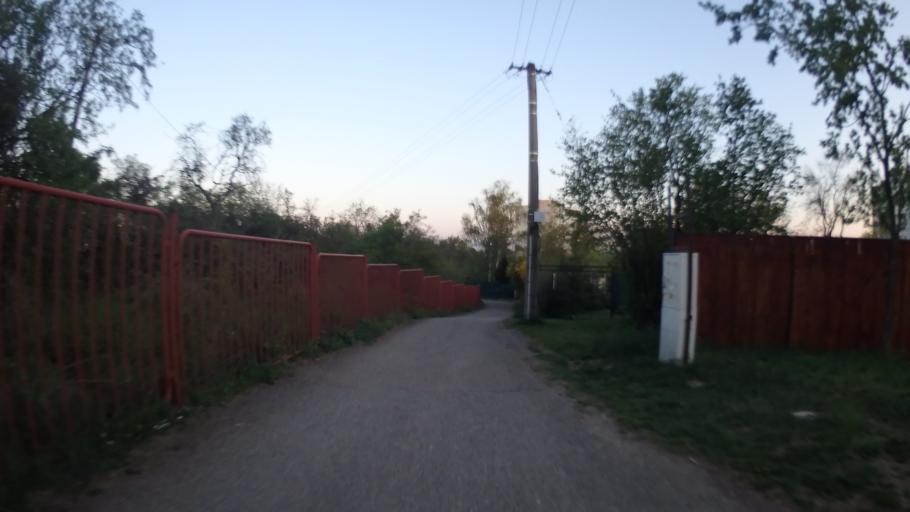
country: CZ
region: South Moravian
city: Ostopovice
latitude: 49.1798
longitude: 16.5546
